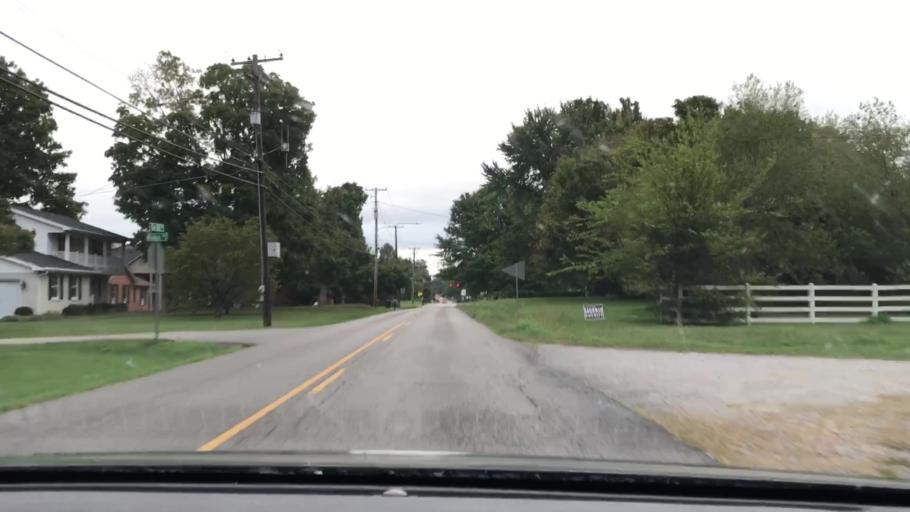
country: US
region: Kentucky
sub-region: Christian County
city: Hopkinsville
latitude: 36.8463
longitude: -87.5143
